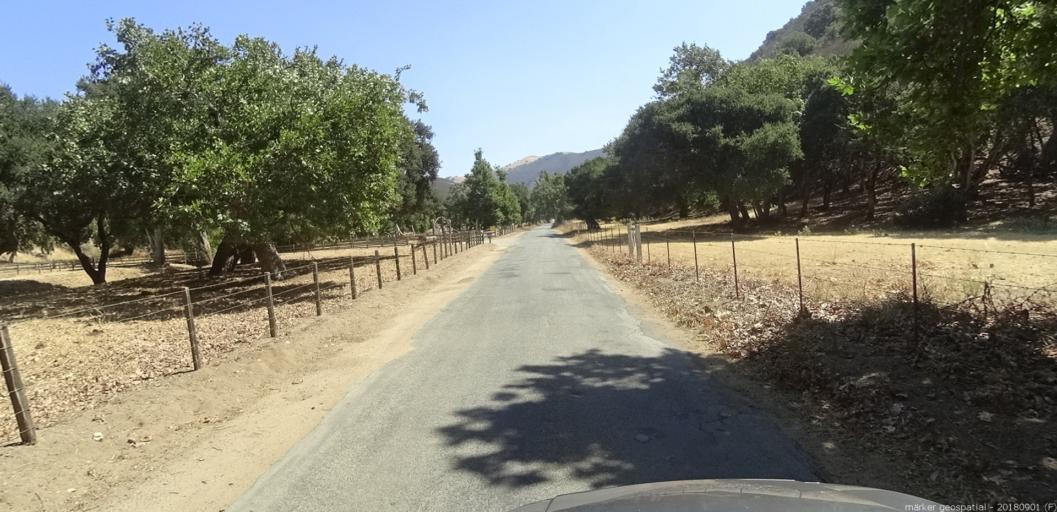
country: US
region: California
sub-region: Monterey County
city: Gonzales
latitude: 36.6033
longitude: -121.4180
